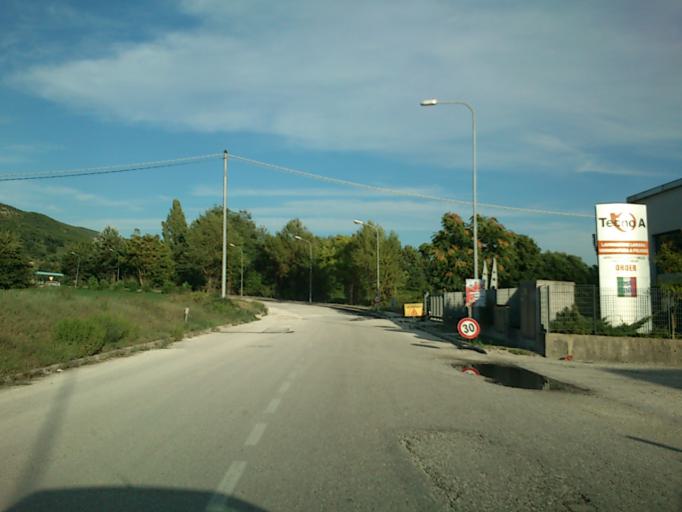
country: IT
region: The Marches
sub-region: Provincia di Pesaro e Urbino
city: Canavaccio
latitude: 43.6902
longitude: 12.7051
